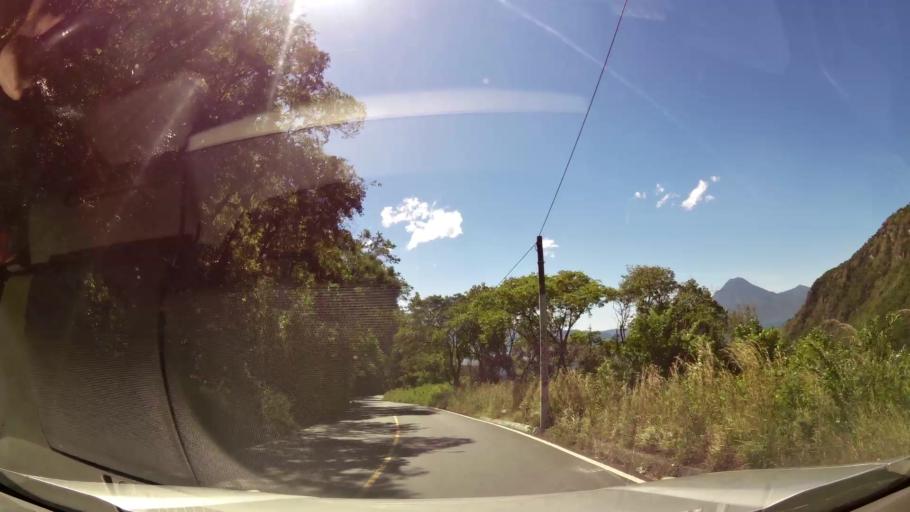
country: GT
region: Solola
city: Panajachel
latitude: 14.7526
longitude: -91.1623
